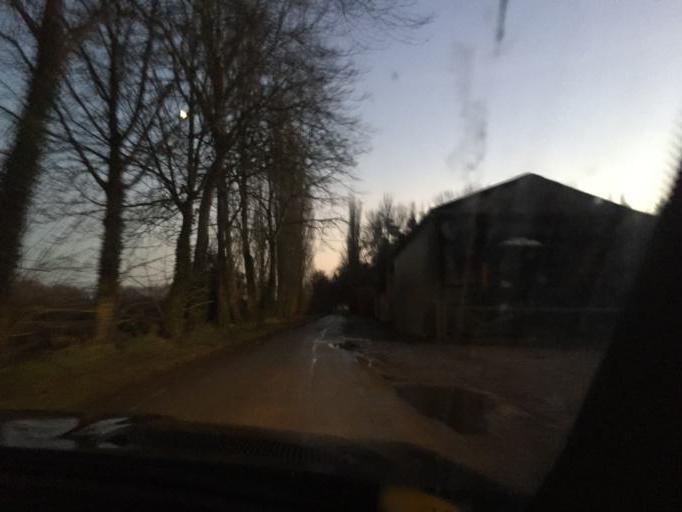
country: GB
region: England
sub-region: Northamptonshire
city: Silverstone
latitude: 52.0829
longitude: -1.0779
